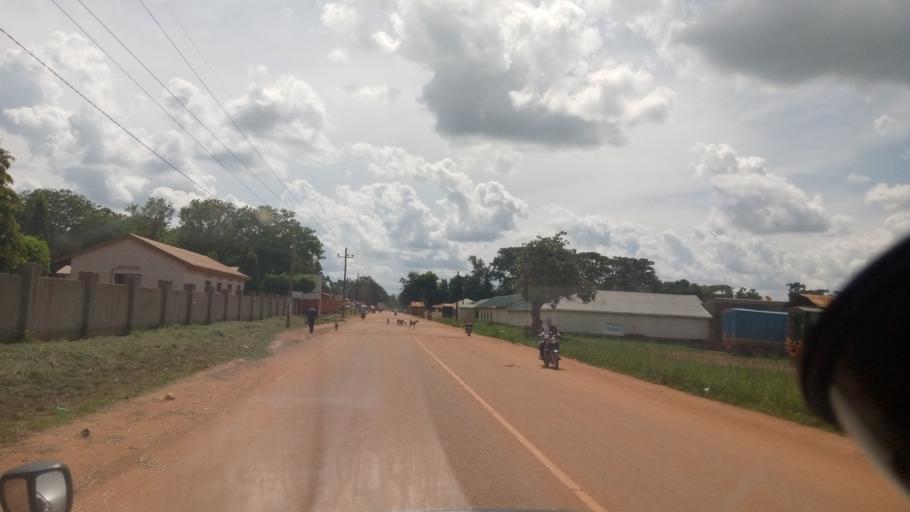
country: UG
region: Northern Region
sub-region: Lira District
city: Lira
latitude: 2.2491
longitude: 32.9042
